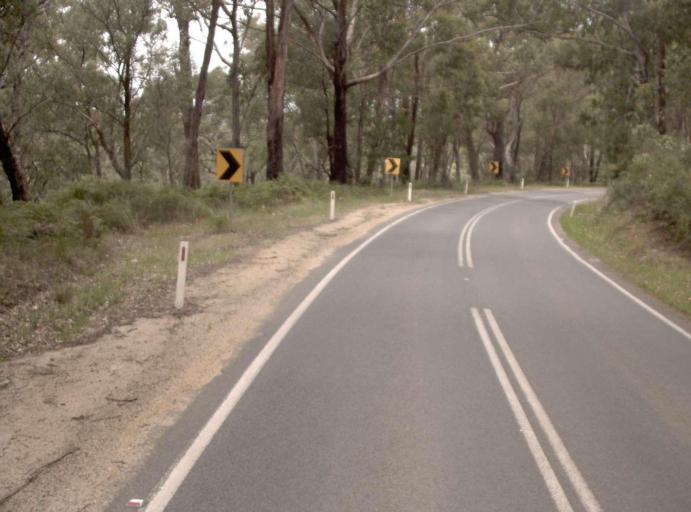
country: AU
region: Victoria
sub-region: Latrobe
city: Traralgon
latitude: -38.4185
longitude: 146.7478
